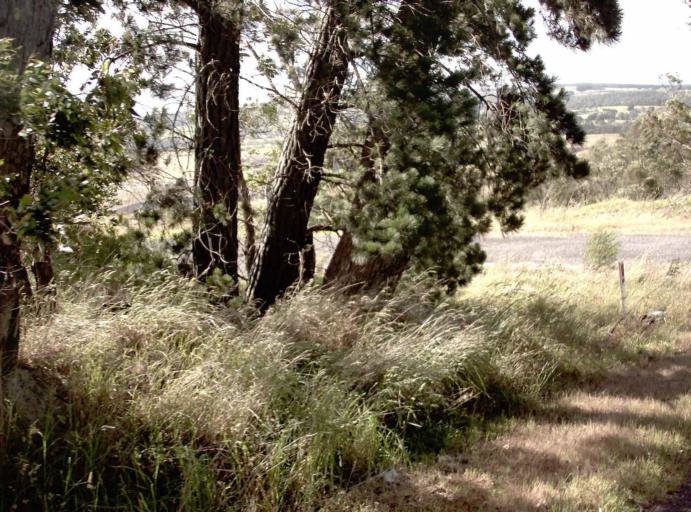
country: AU
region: Victoria
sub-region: Latrobe
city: Morwell
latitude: -38.1820
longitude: 146.4043
